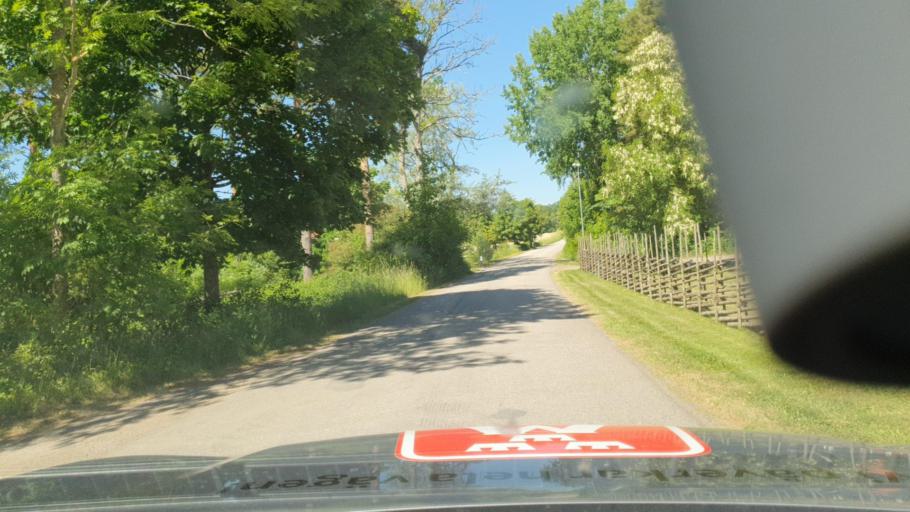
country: SE
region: Kalmar
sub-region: Emmaboda Kommun
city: Emmaboda
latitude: 56.5272
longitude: 15.6032
